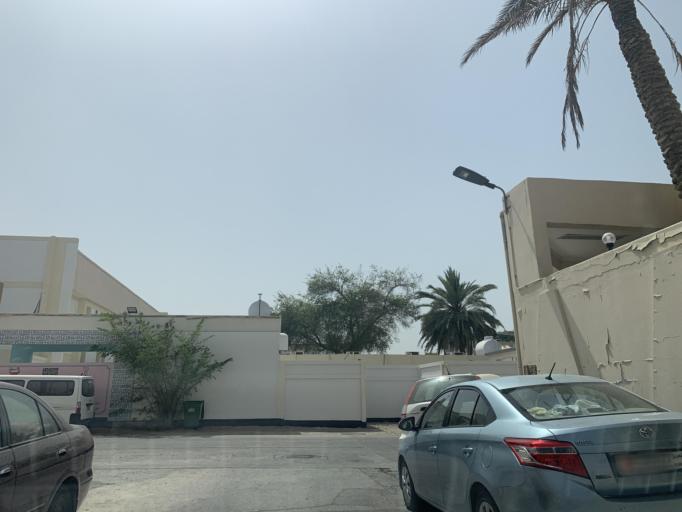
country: BH
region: Northern
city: Madinat `Isa
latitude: 26.1531
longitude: 50.5250
